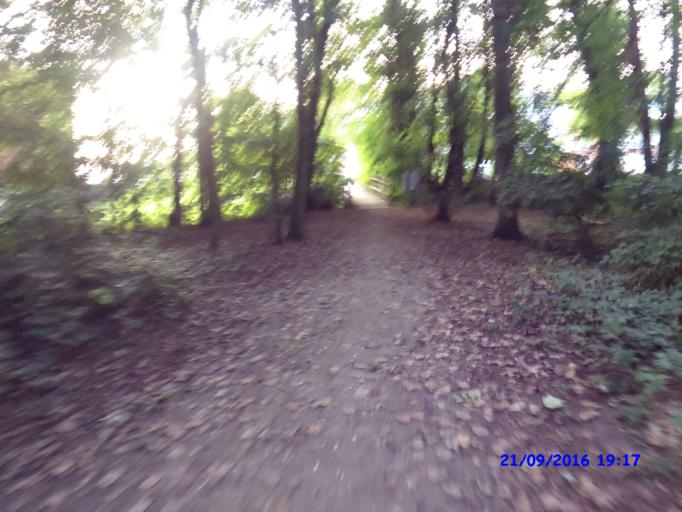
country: BE
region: Flanders
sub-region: Provincie Antwerpen
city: Wijnegem
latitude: 51.2256
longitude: 4.5240
